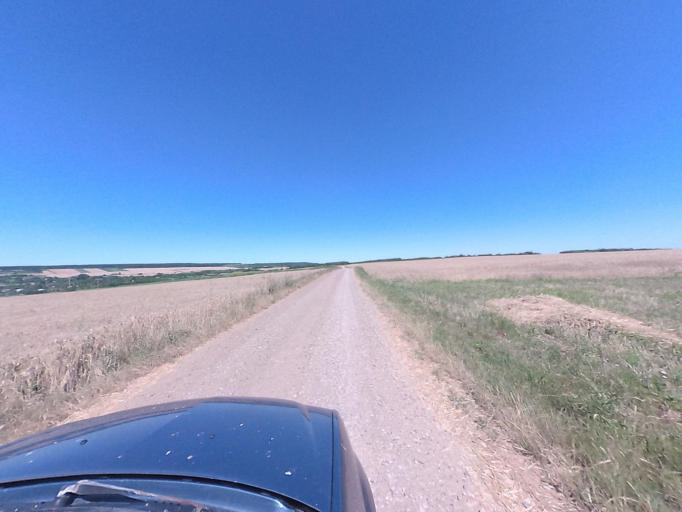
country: RO
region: Vaslui
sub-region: Comuna Costesti
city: Costesti
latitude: 46.4803
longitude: 27.7767
